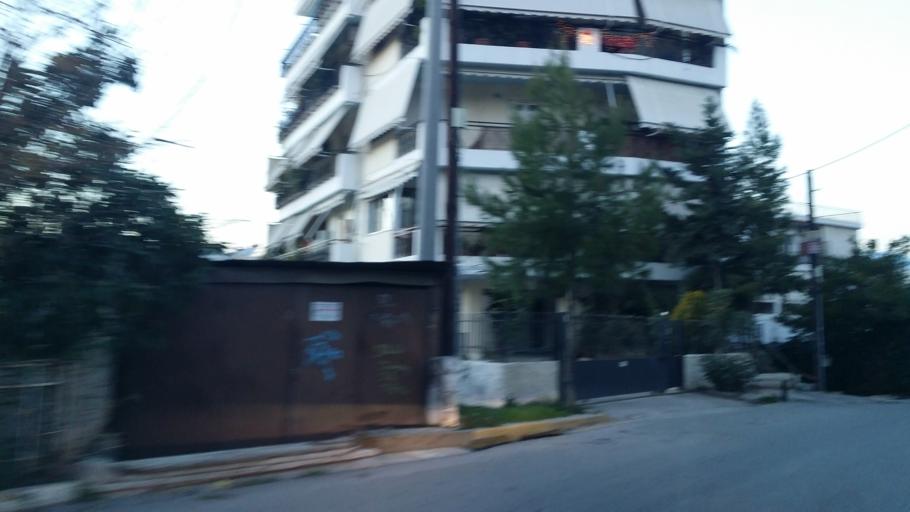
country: GR
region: Attica
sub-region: Nomarchia Athinas
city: Irakleio
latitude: 38.0575
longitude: 23.7591
